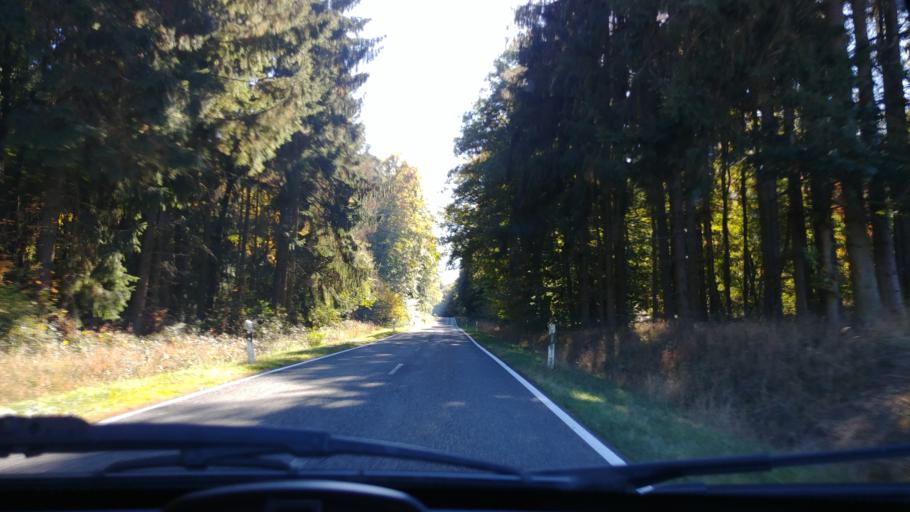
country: DE
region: Hesse
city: Burg Hohenstein
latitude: 50.1789
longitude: 8.1027
